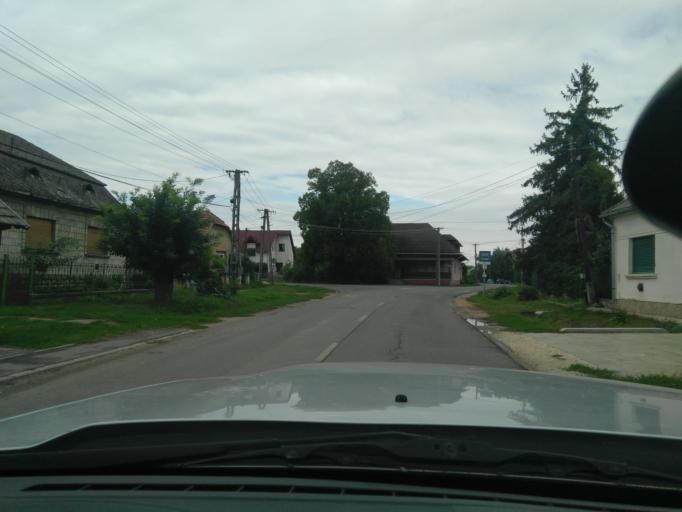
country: HU
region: Fejer
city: Val
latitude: 47.3707
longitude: 18.7416
